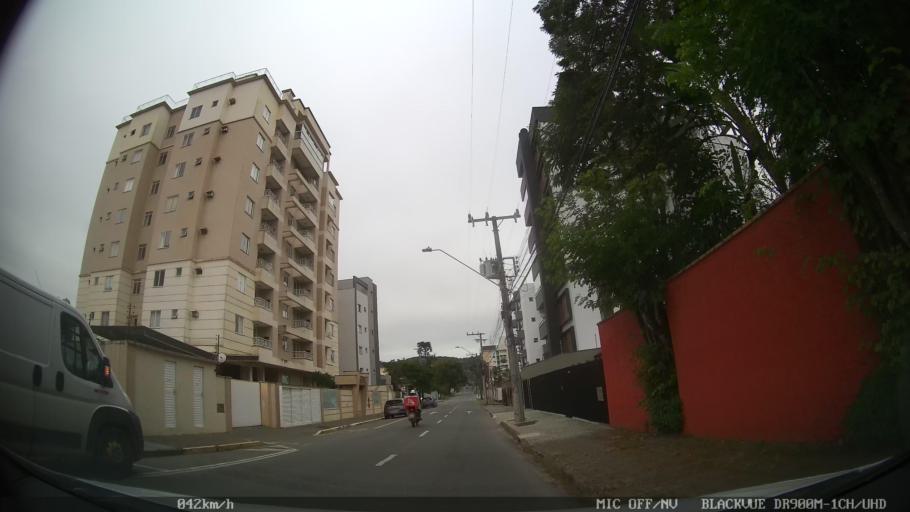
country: BR
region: Santa Catarina
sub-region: Joinville
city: Joinville
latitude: -26.2640
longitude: -48.8497
